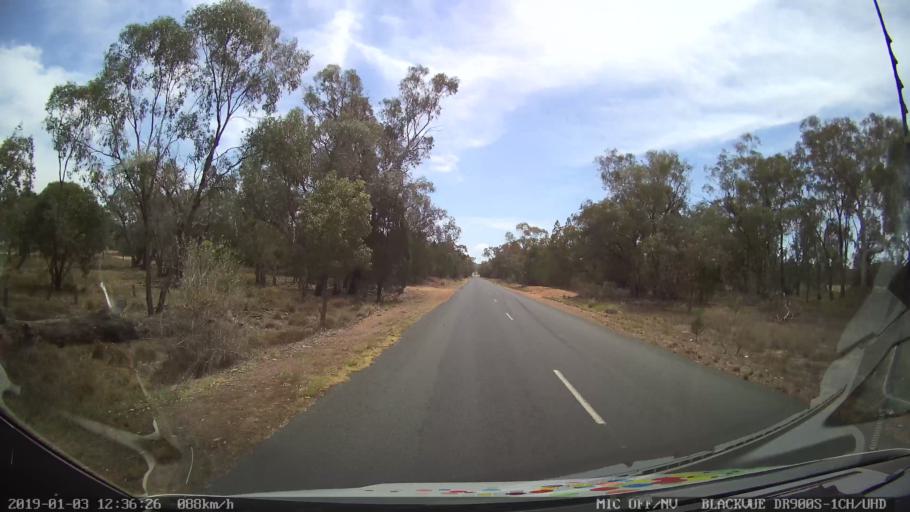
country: AU
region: New South Wales
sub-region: Weddin
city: Grenfell
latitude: -33.8549
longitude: 148.1769
